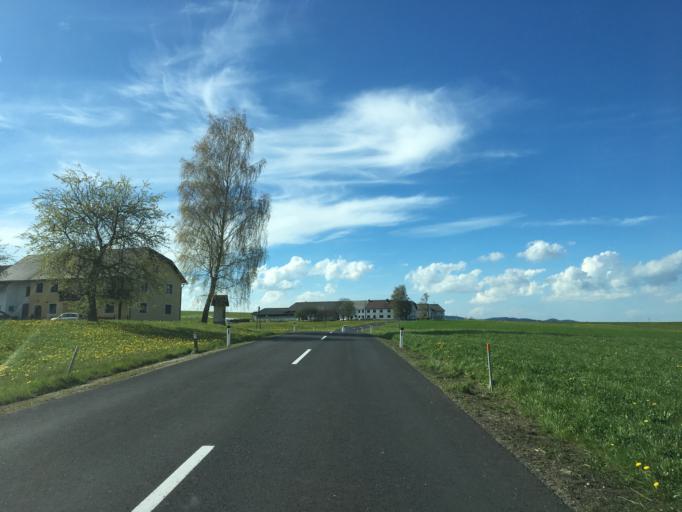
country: AT
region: Upper Austria
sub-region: Politischer Bezirk Urfahr-Umgebung
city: Reichenau im Muhlkreis
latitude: 48.4768
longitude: 14.3342
